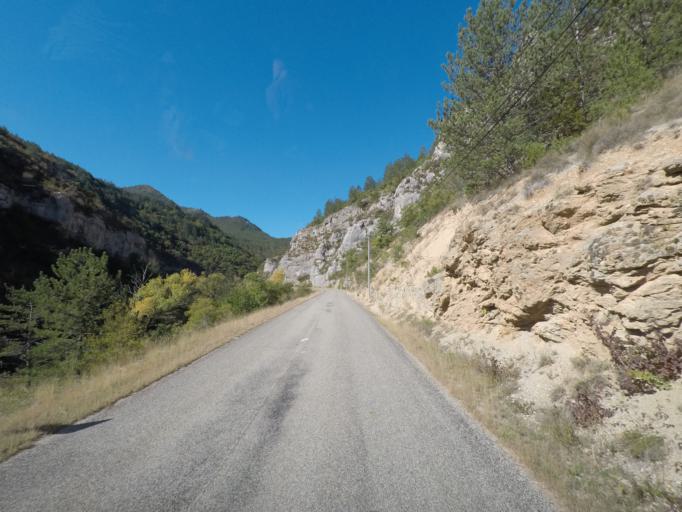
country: FR
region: Rhone-Alpes
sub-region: Departement de la Drome
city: Die
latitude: 44.6314
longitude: 5.3007
